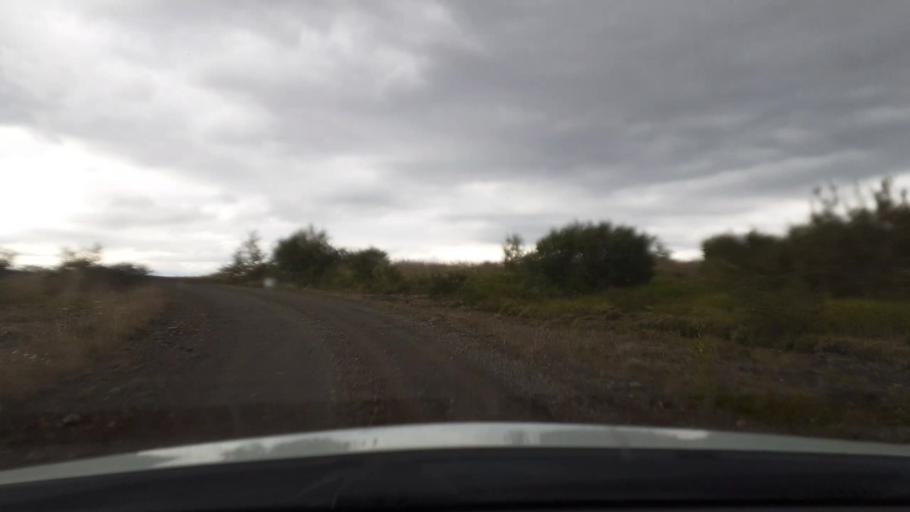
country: IS
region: West
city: Borgarnes
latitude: 64.6428
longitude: -21.7583
